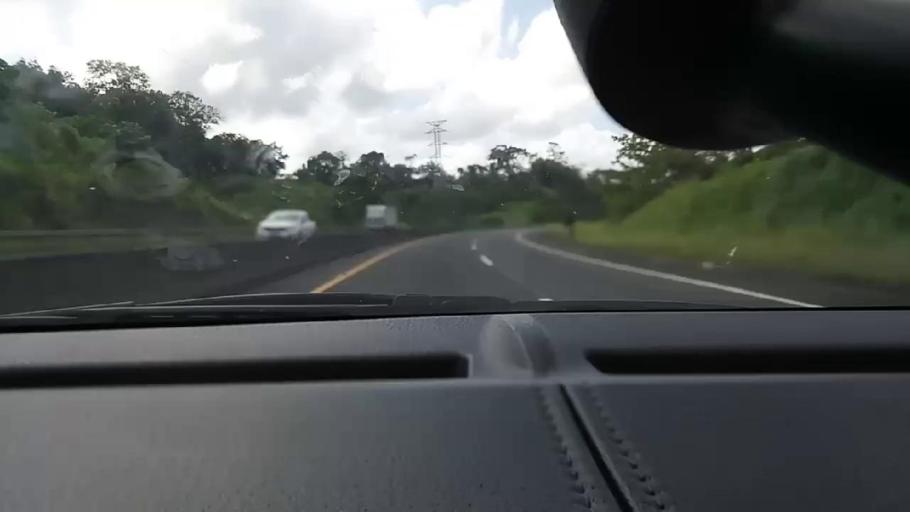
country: PA
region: Colon
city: Las Margaritas
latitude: 9.3318
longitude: -79.8638
